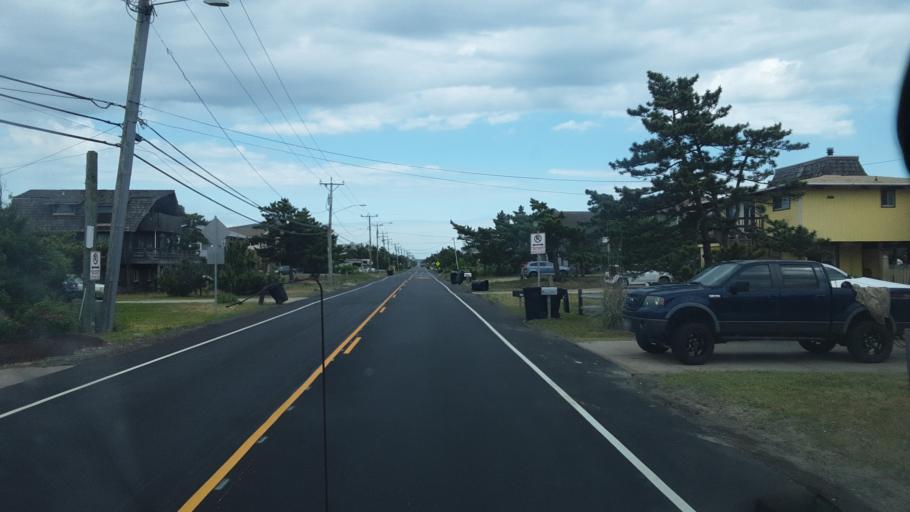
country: US
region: Virginia
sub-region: City of Virginia Beach
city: Virginia Beach
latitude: 36.7183
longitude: -75.9346
